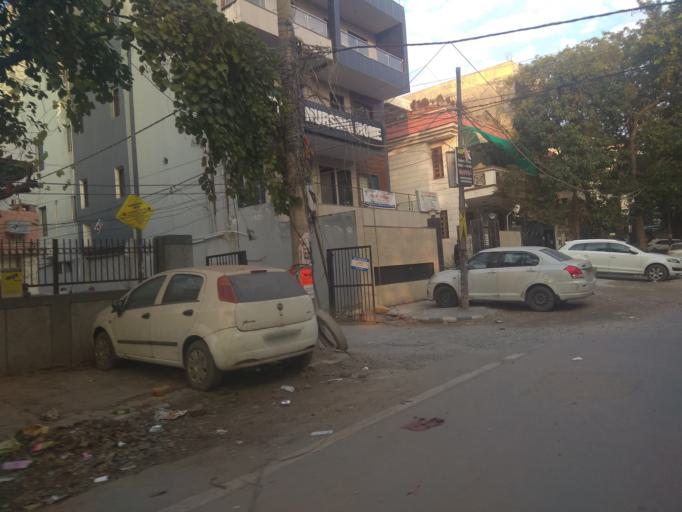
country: IN
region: NCT
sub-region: West Delhi
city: Nangloi Jat
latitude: 28.6316
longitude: 77.0713
